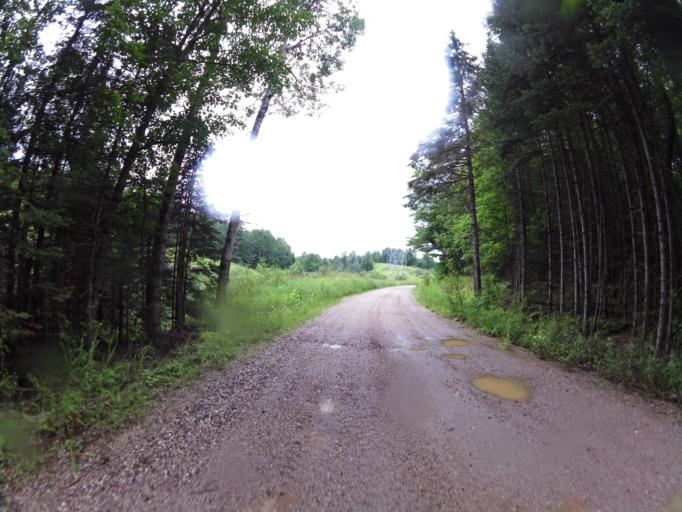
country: CA
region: Ontario
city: Renfrew
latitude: 45.0760
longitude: -76.7222
